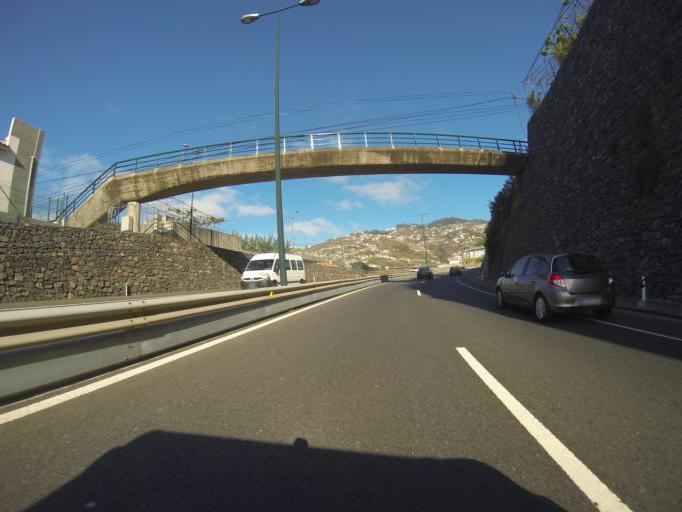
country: PT
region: Madeira
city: Camara de Lobos
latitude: 32.6584
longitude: -16.9748
